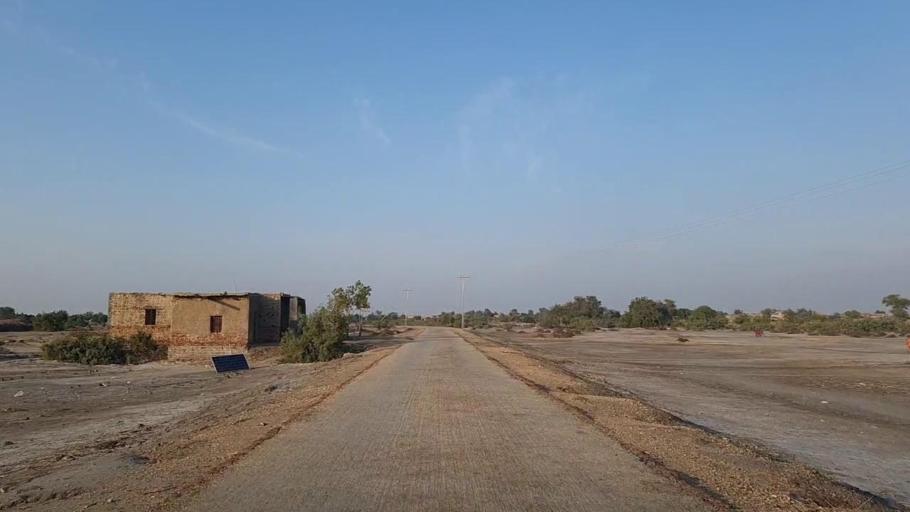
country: PK
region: Sindh
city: Jam Sahib
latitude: 26.3771
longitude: 68.5386
